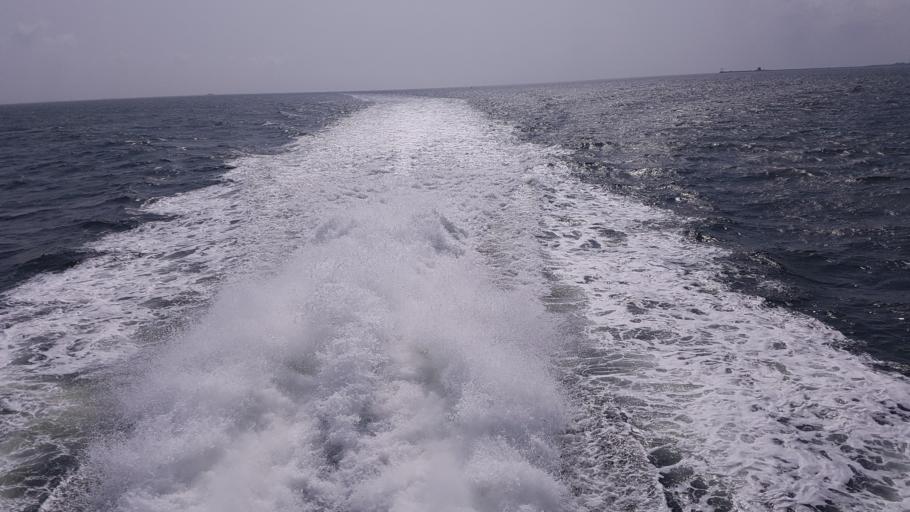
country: DE
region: Schleswig-Holstein
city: Pellworm
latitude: 54.5208
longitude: 8.7413
